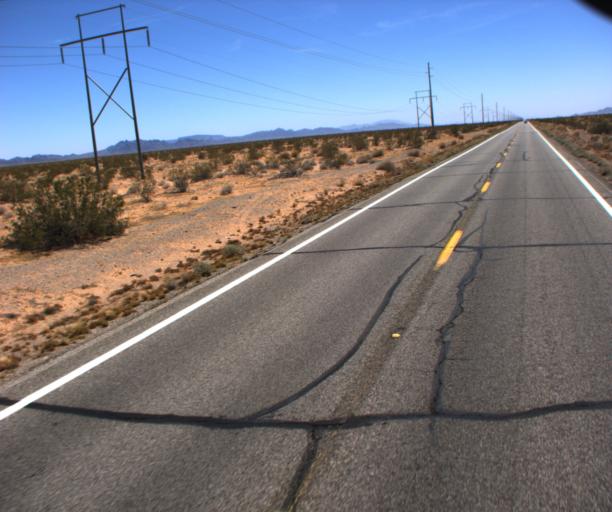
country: US
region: Arizona
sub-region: La Paz County
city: Quartzsite
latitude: 33.8849
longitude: -114.2170
